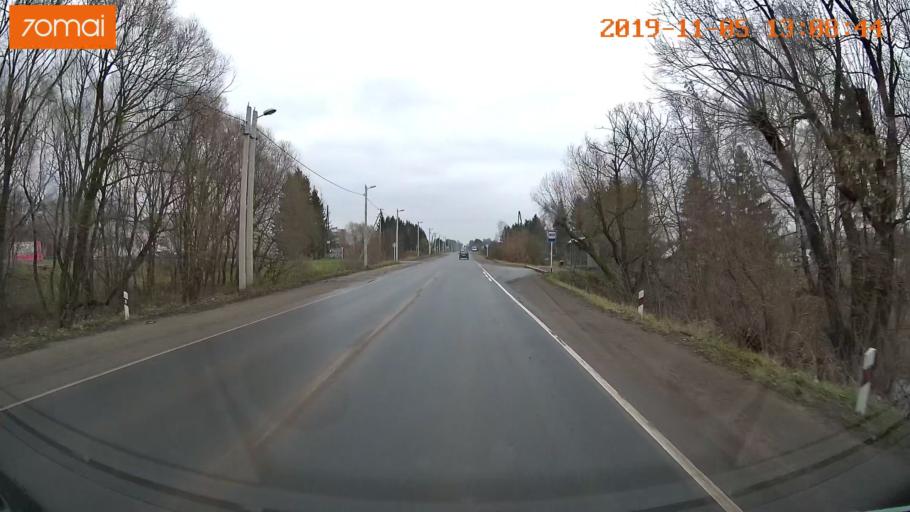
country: RU
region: Ivanovo
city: Kitovo
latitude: 56.8637
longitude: 41.2959
